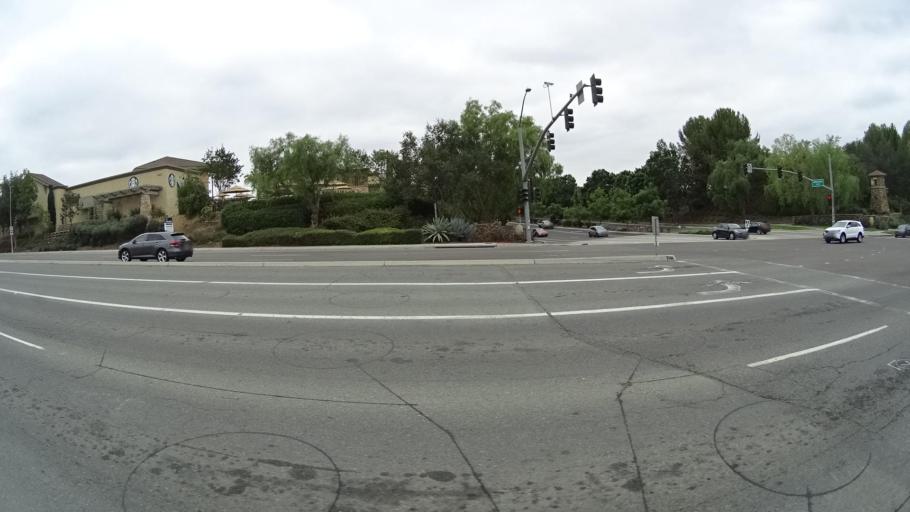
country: US
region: California
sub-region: San Diego County
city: Fairbanks Ranch
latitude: 33.0166
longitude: -117.1110
